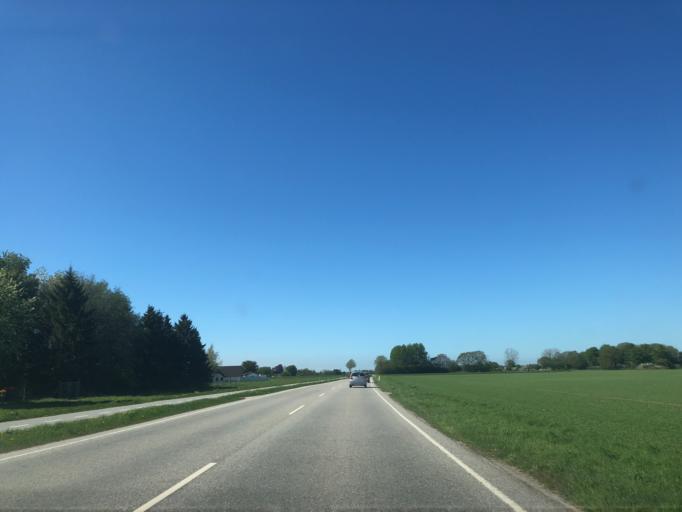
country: DK
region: Zealand
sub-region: Stevns Kommune
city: Store Heddinge
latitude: 55.3422
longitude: 12.3404
